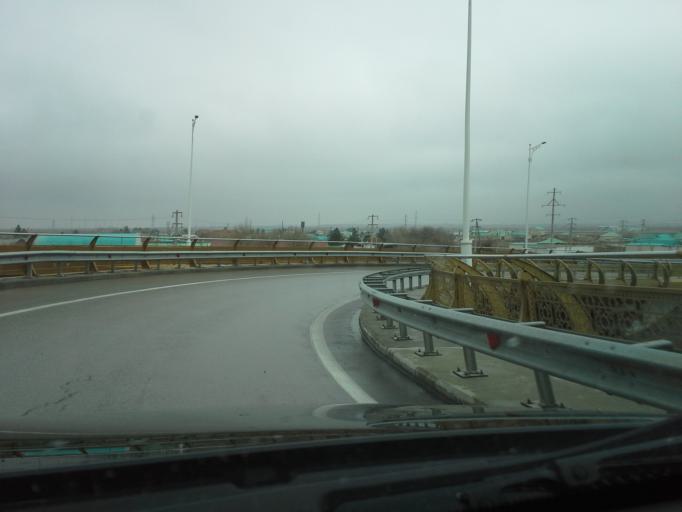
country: TM
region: Ahal
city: Ashgabat
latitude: 37.9513
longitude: 58.4378
